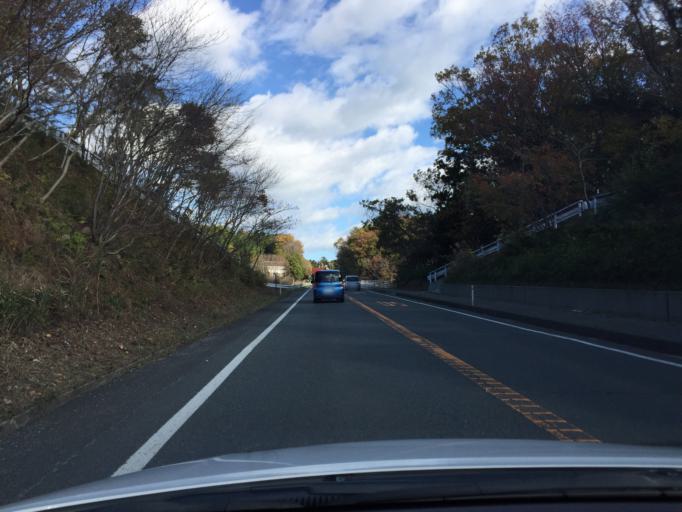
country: JP
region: Fukushima
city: Namie
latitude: 37.3272
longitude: 141.0157
